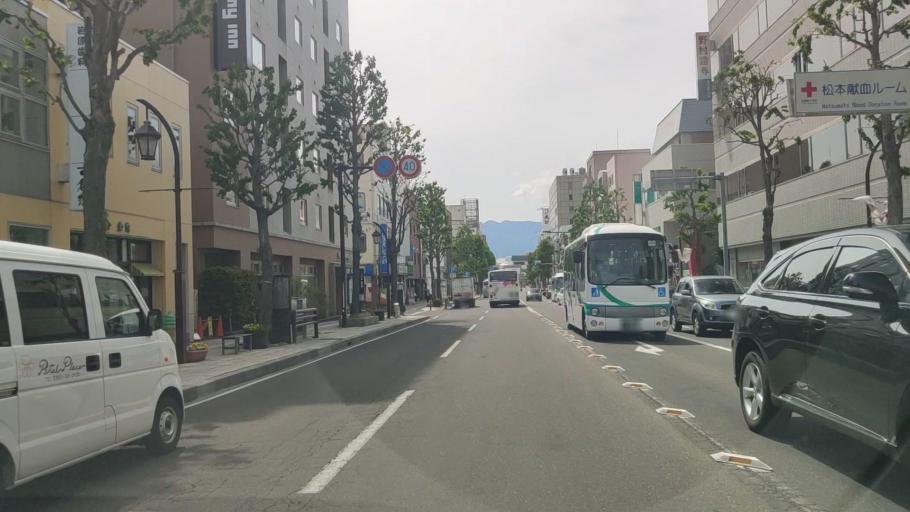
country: JP
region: Nagano
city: Matsumoto
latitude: 36.2311
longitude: 137.9692
